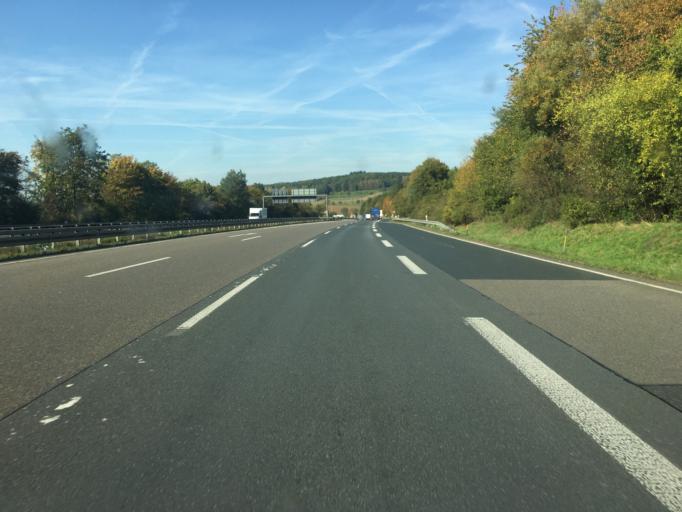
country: DE
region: Hesse
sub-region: Regierungsbezirk Giessen
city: Asslar
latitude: 50.5989
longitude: 8.4792
